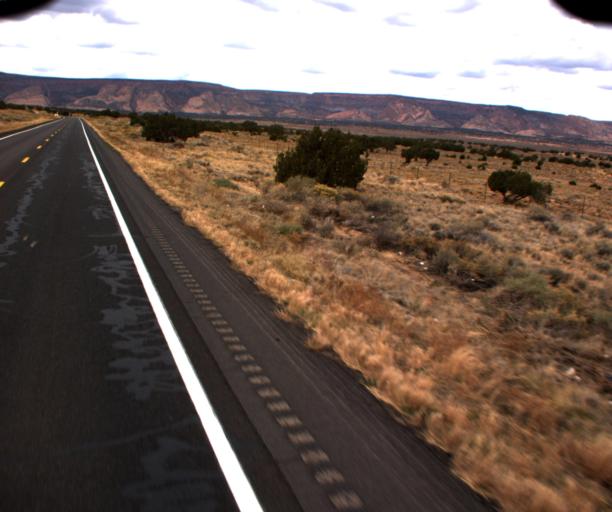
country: US
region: Arizona
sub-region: Navajo County
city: Kayenta
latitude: 36.6986
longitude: -110.3309
